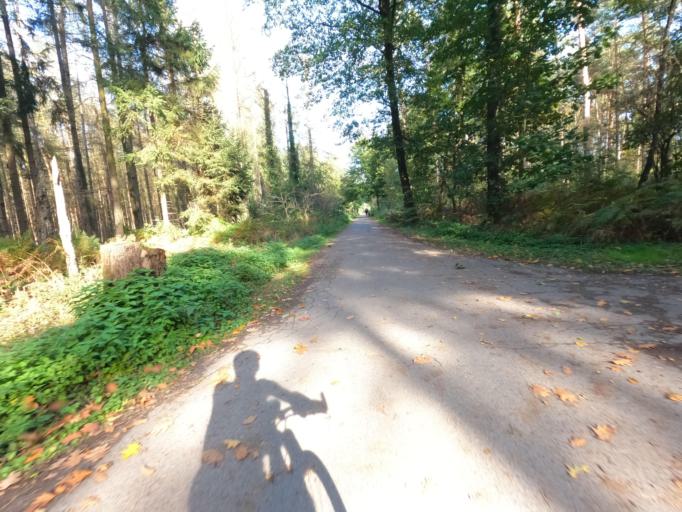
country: DE
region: North Rhine-Westphalia
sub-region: Regierungsbezirk Koln
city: Wassenberg
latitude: 51.1320
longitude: 6.1850
